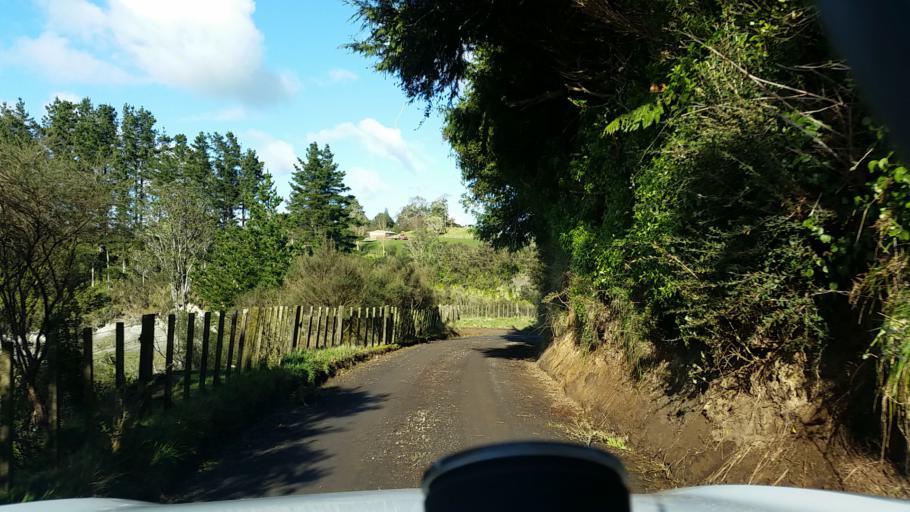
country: NZ
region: Taranaki
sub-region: South Taranaki District
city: Eltham
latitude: -39.4581
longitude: 174.3699
